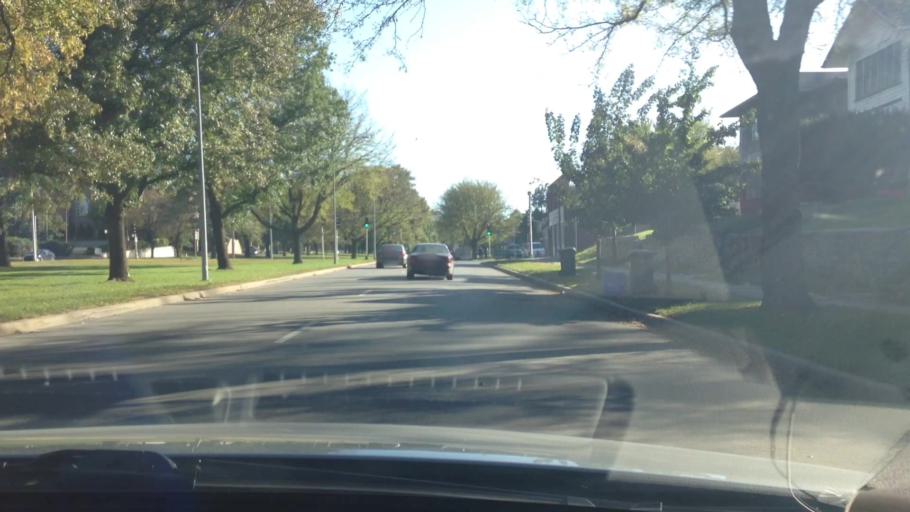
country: US
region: Kansas
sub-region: Johnson County
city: Mission Hills
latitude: 39.0279
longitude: -94.5680
